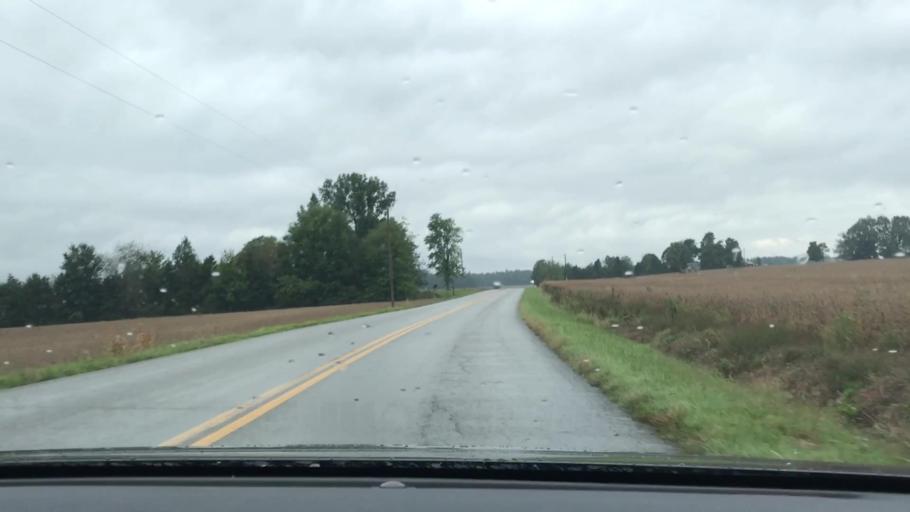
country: US
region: Kentucky
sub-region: McLean County
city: Calhoun
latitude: 37.3977
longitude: -87.2780
